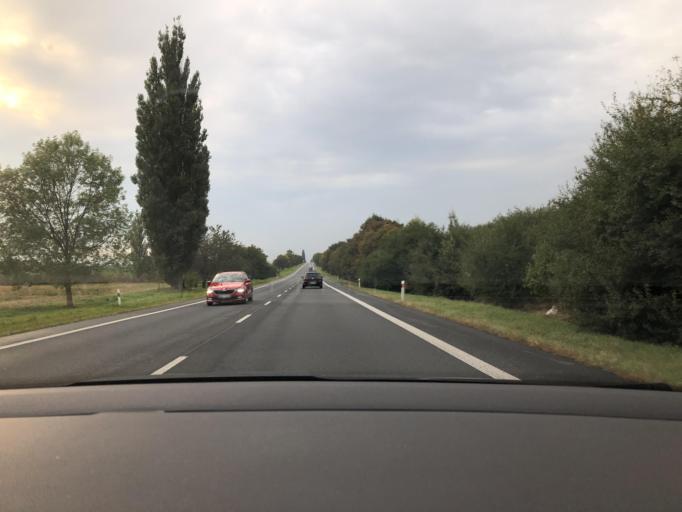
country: CZ
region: Central Bohemia
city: Velim
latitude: 50.0408
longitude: 15.1018
